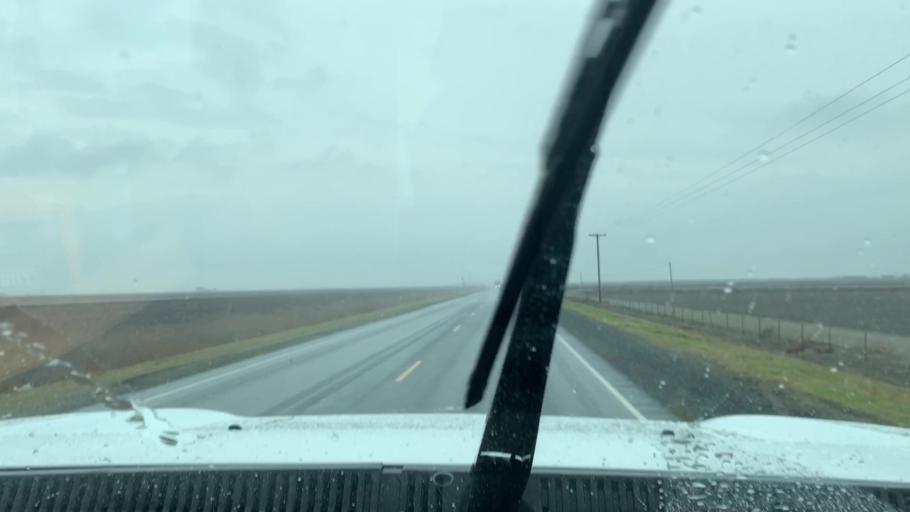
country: US
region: California
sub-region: Tulare County
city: Alpaugh
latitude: 35.9222
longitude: -119.4277
